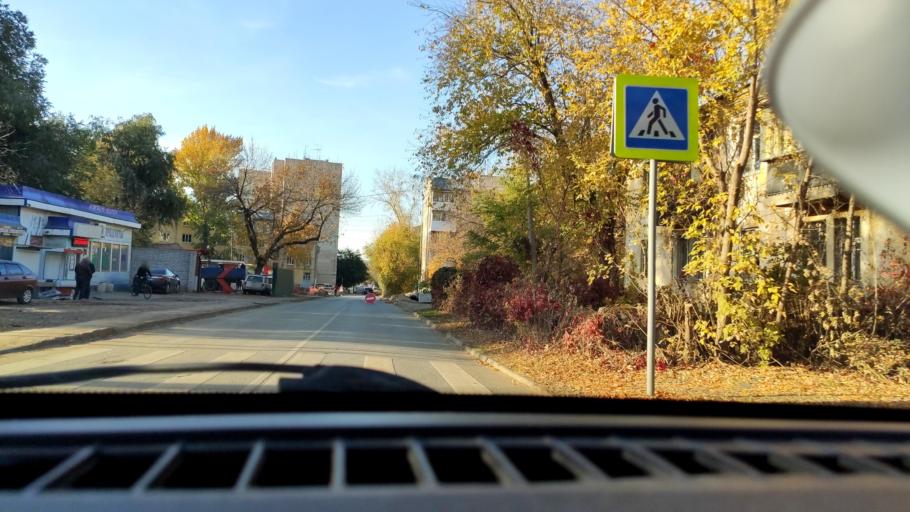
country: RU
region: Samara
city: Samara
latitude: 53.2304
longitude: 50.1859
